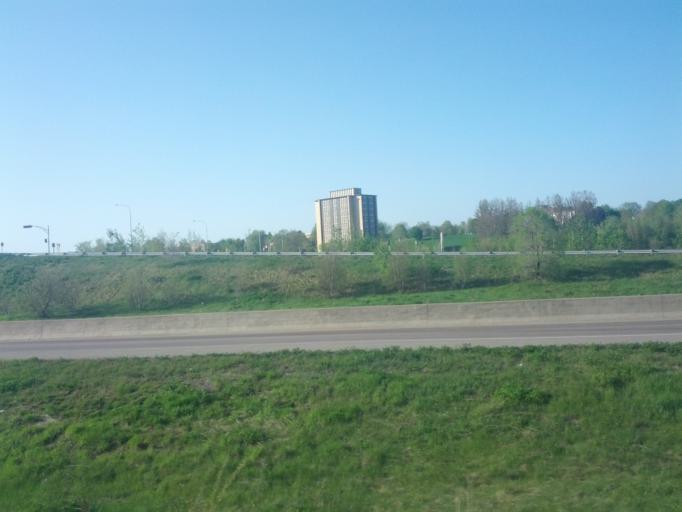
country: CA
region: New Brunswick
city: Moncton
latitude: 46.0996
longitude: -64.7849
